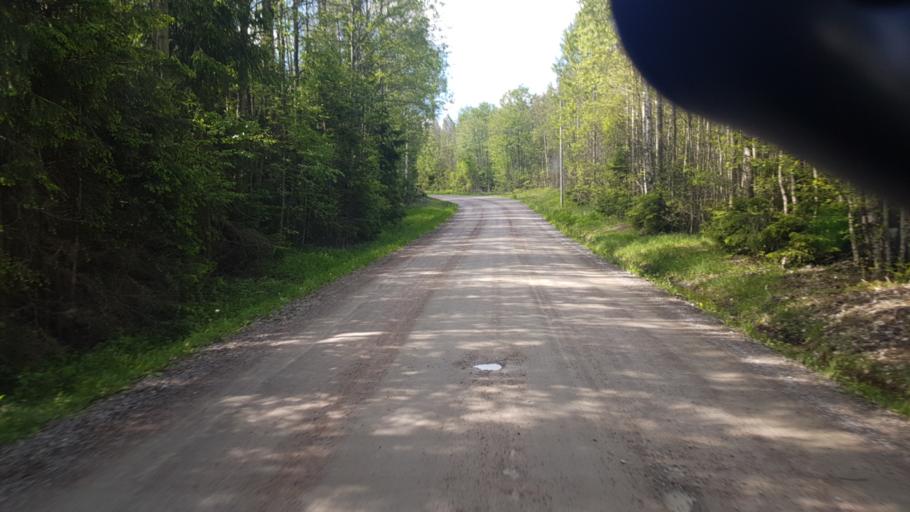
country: SE
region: Vaermland
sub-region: Arvika Kommun
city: Arvika
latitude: 59.5218
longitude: 12.7347
